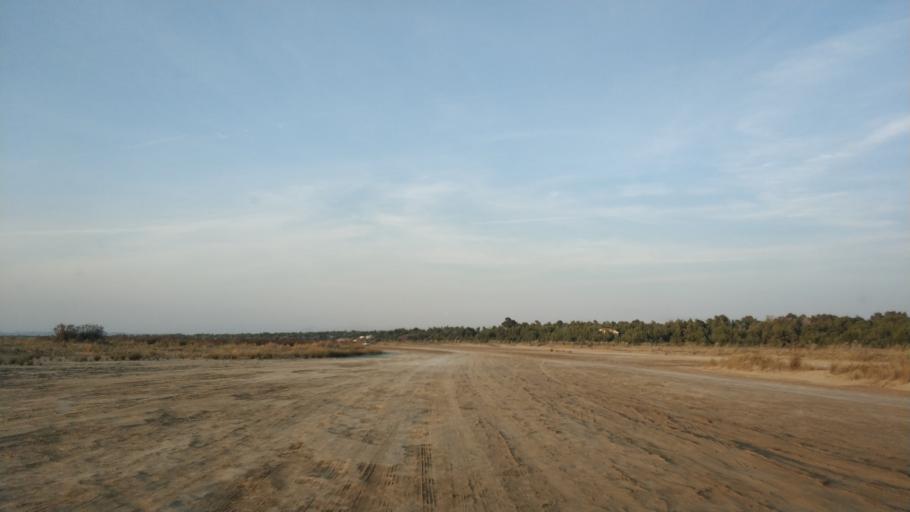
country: AL
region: Fier
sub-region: Rrethi i Lushnjes
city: Divjake
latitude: 40.9601
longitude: 19.4717
